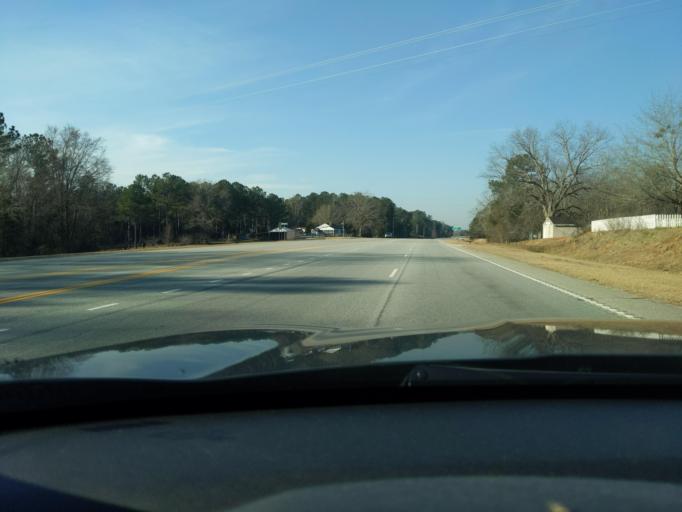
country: US
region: South Carolina
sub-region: Abbeville County
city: Abbeville
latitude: 34.1236
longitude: -82.4446
